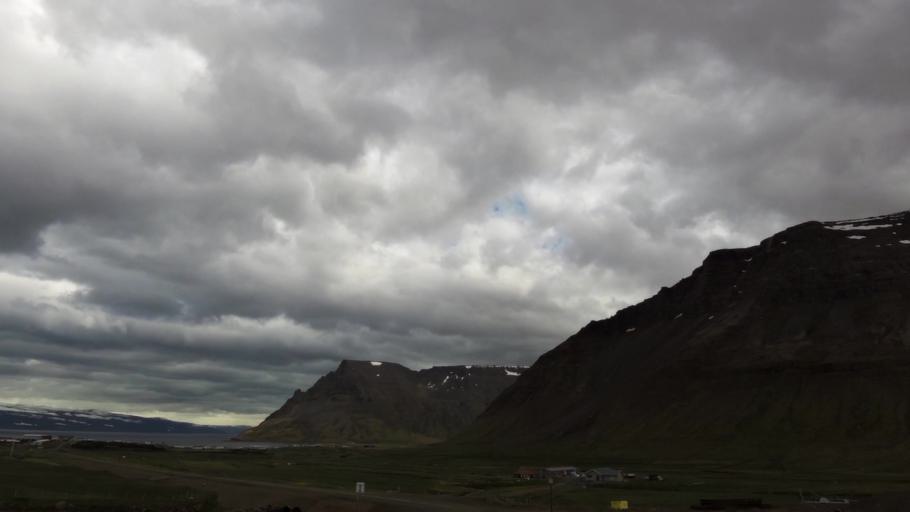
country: IS
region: Westfjords
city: Isafjoerdur
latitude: 66.1581
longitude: -23.2926
